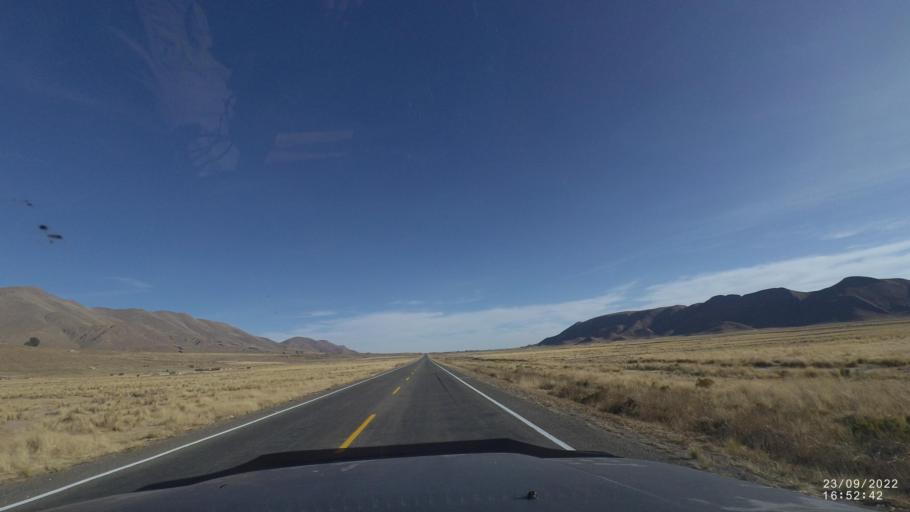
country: BO
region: Oruro
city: Poopo
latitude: -18.4355
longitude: -66.9730
